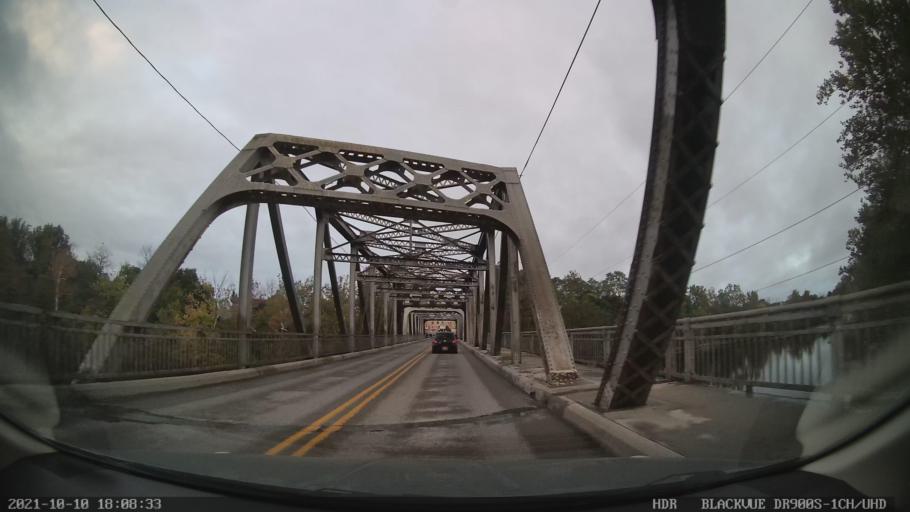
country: US
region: Pennsylvania
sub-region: Lehigh County
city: Cementon
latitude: 40.6896
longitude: -75.5050
